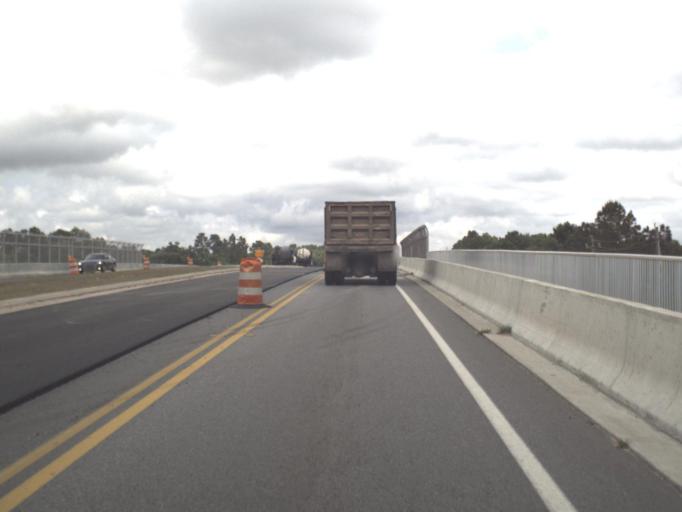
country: US
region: Florida
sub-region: Santa Rosa County
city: Bagdad
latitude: 30.5685
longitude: -87.0869
